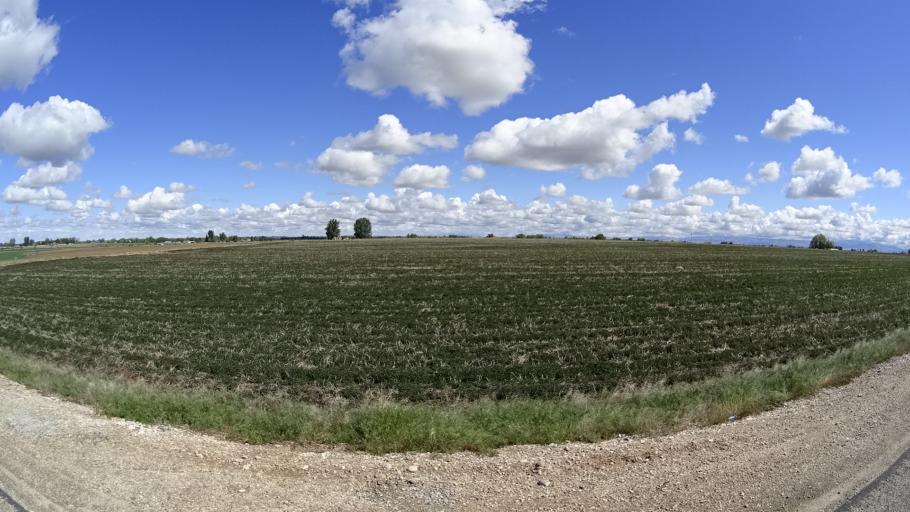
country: US
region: Idaho
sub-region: Ada County
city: Kuna
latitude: 43.5102
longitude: -116.4423
